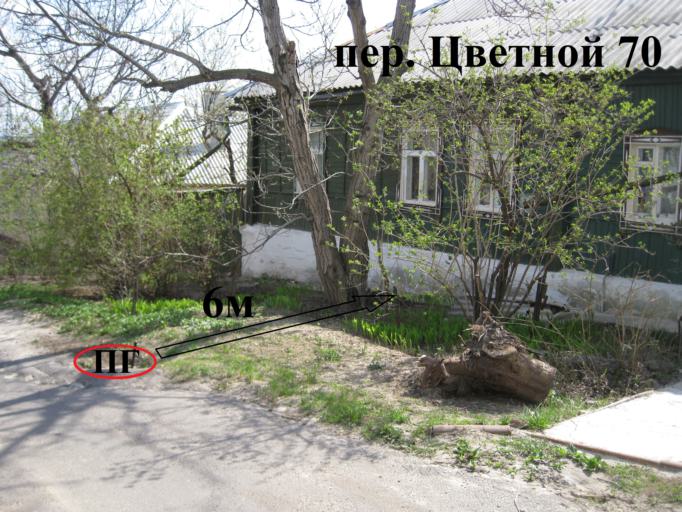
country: RU
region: Voronezj
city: Voronezh
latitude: 51.6402
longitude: 39.1986
